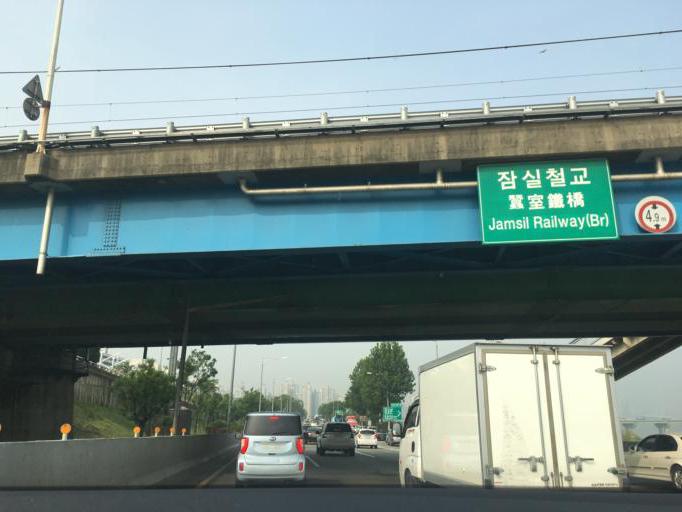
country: KR
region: Gyeonggi-do
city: Guri-si
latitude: 37.5238
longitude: 127.1024
